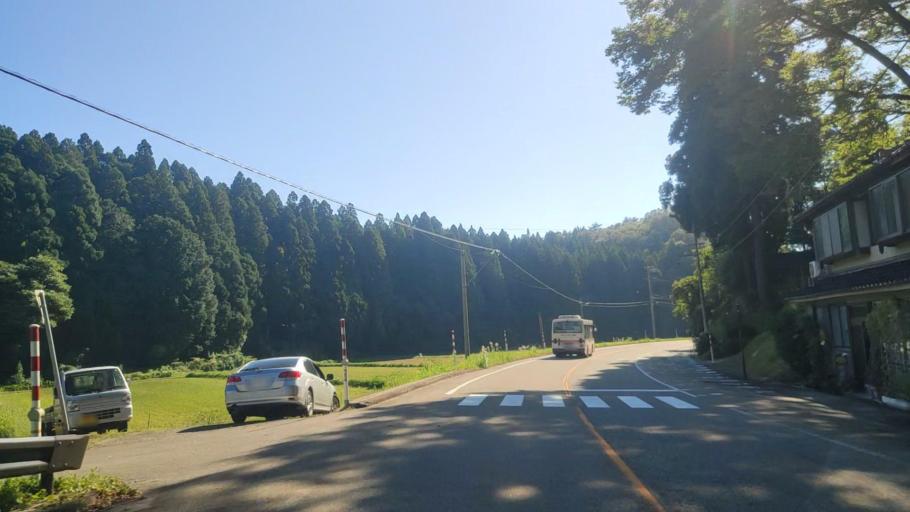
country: JP
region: Ishikawa
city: Nanao
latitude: 37.2503
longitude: 136.9988
